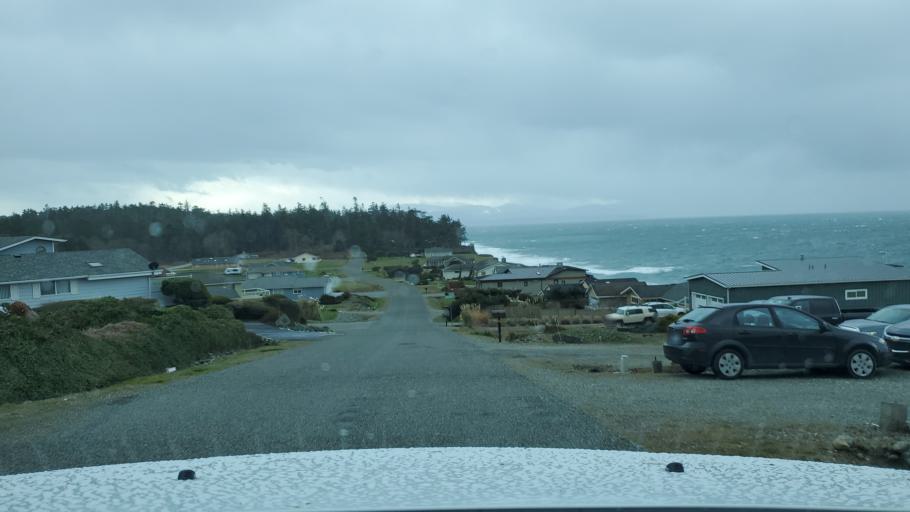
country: US
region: Washington
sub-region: Island County
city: Coupeville
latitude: 48.2368
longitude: -122.7621
